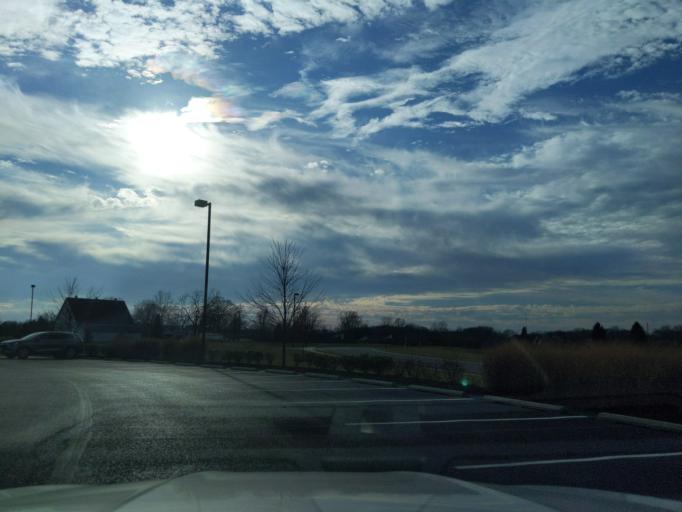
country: US
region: Indiana
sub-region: Decatur County
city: Greensburg
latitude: 39.3208
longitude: -85.4672
